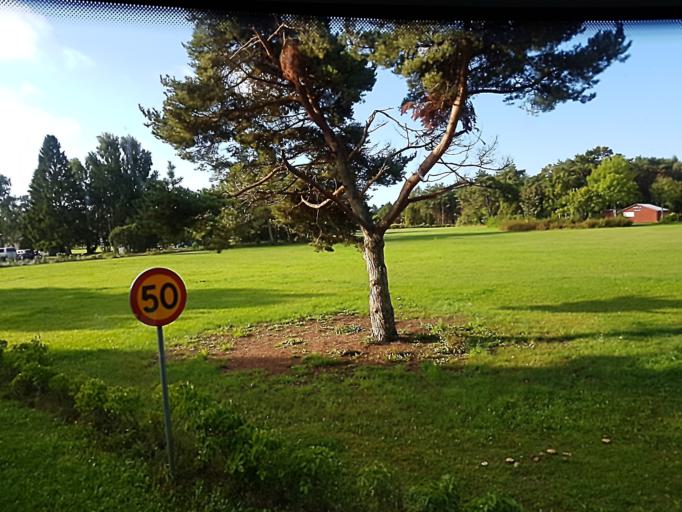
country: SE
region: Gotland
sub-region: Gotland
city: Klintehamn
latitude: 57.4862
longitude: 18.1387
